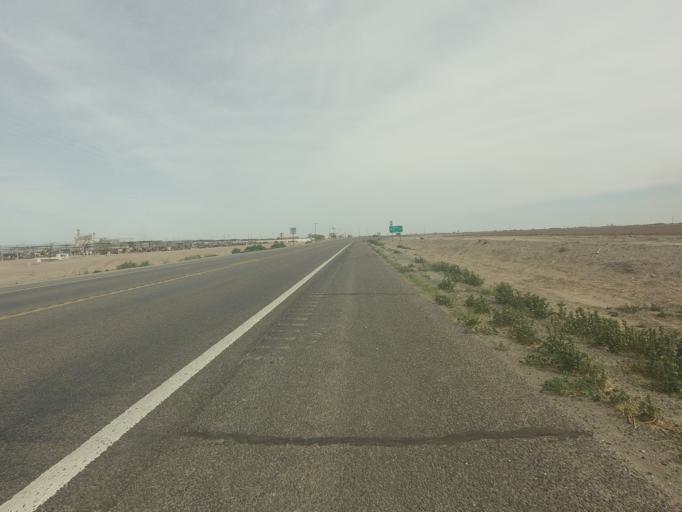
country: US
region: California
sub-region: Imperial County
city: Brawley
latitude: 32.9744
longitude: -115.4111
